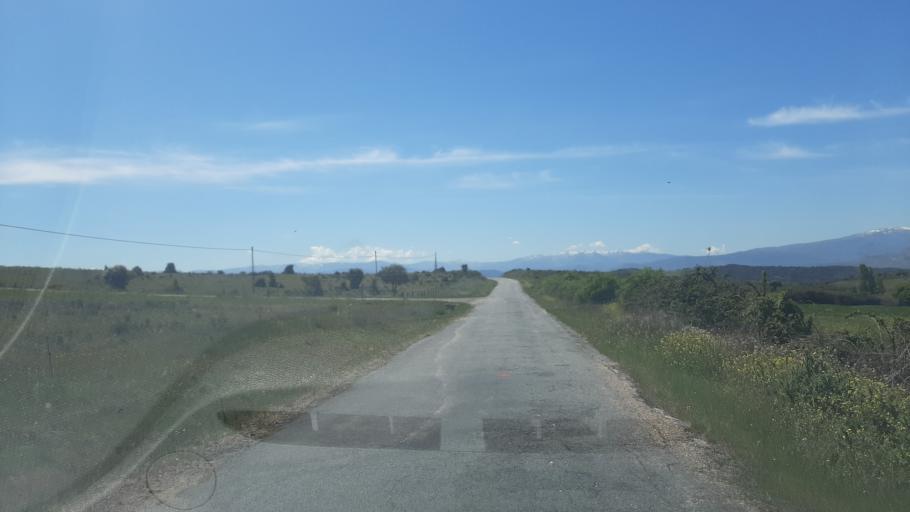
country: ES
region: Castille and Leon
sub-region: Provincia de Avila
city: Narrillos del Alamo
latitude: 40.5603
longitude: -5.4396
